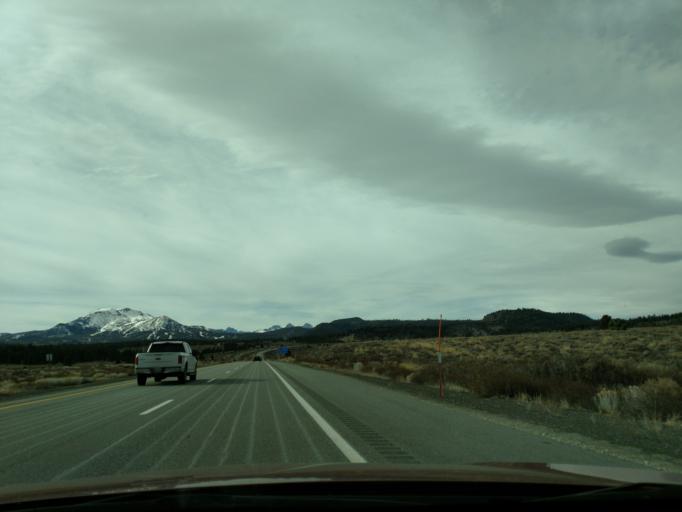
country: US
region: California
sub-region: Mono County
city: Mammoth Lakes
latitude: 37.6374
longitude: -118.8983
